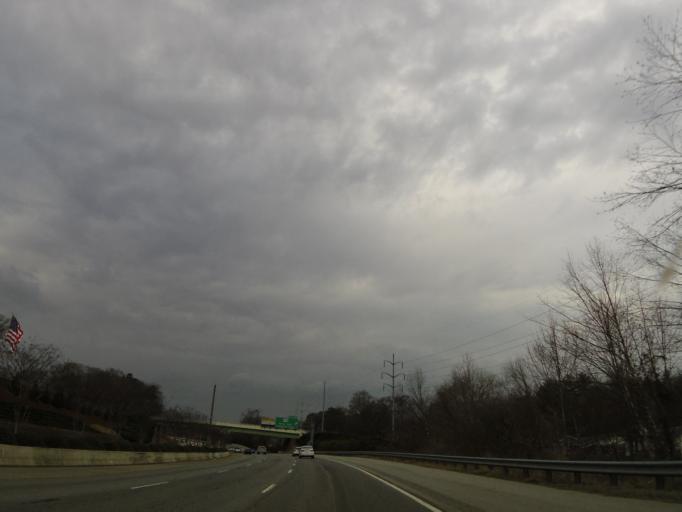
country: US
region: South Carolina
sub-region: Greenville County
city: Greenville
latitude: 34.8534
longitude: -82.3759
